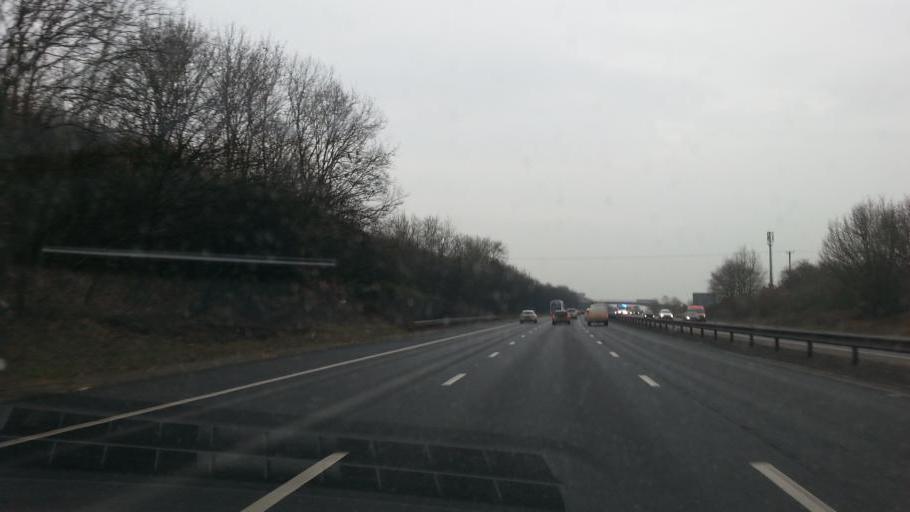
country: GB
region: England
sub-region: Essex
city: Harlow
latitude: 51.7588
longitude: 0.1478
